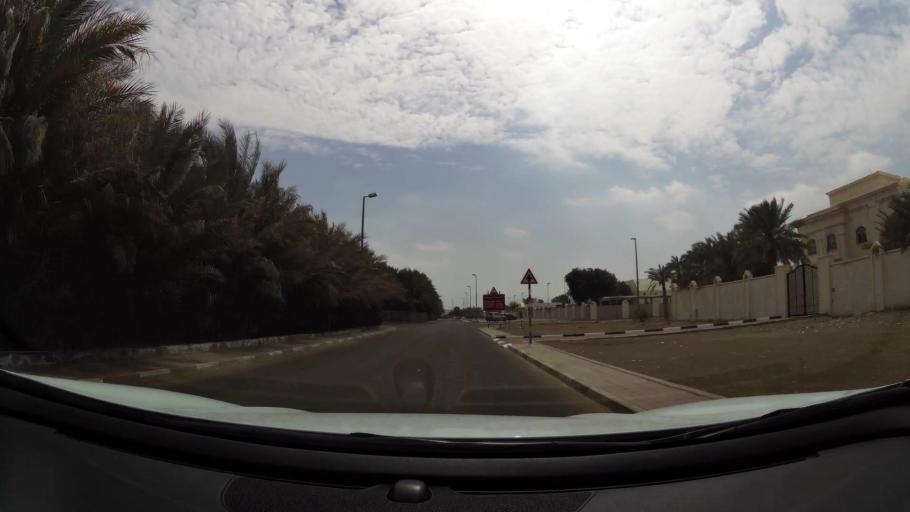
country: AE
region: Abu Dhabi
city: Al Ain
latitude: 24.1999
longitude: 55.7986
